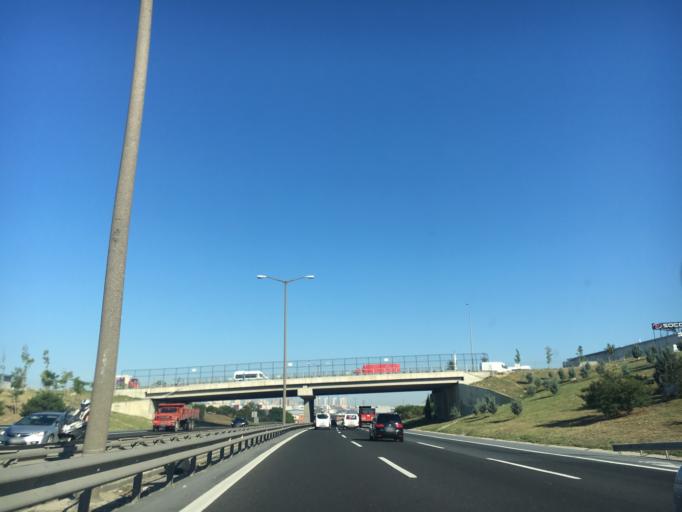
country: TR
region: Istanbul
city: Esenyurt
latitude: 41.0560
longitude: 28.6628
